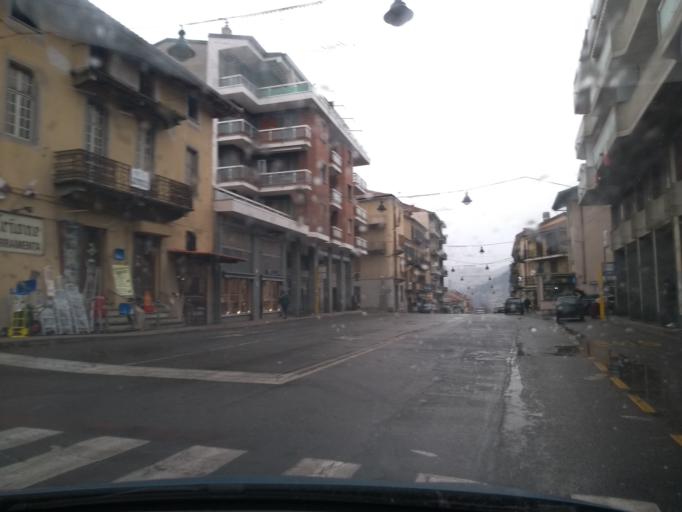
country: IT
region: Piedmont
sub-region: Provincia di Torino
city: Cuorgne
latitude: 45.3912
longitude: 7.6503
